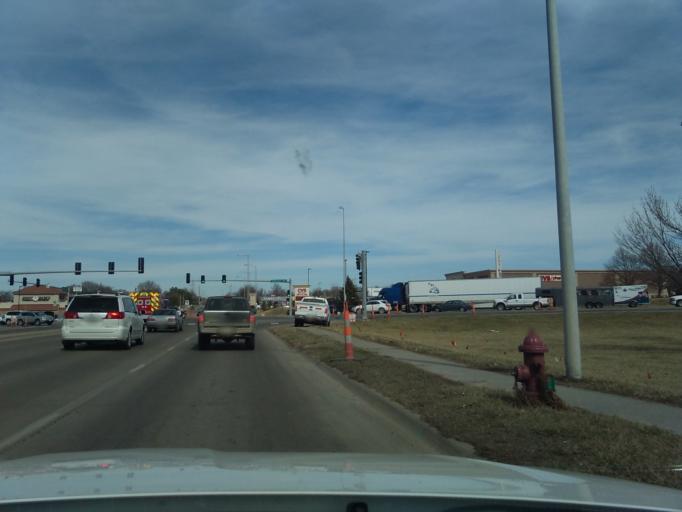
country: US
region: Nebraska
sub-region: Lancaster County
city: Lincoln
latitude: 40.7554
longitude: -96.6444
